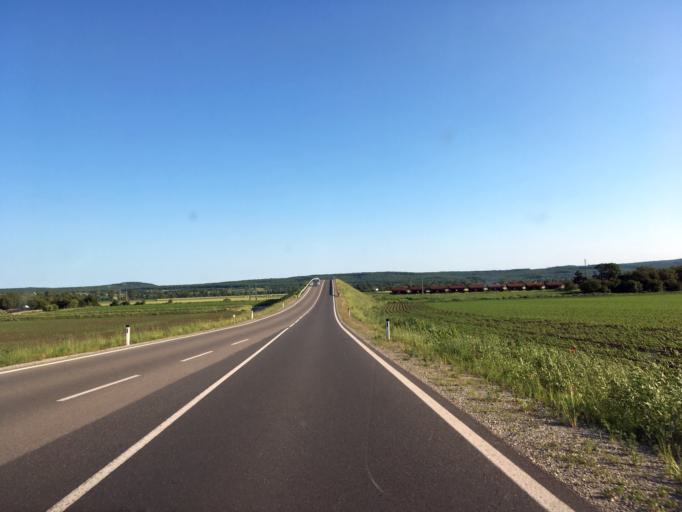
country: AT
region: Lower Austria
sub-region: Politischer Bezirk Bruck an der Leitha
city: Bruck an der Leitha
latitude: 48.0241
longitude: 16.7406
